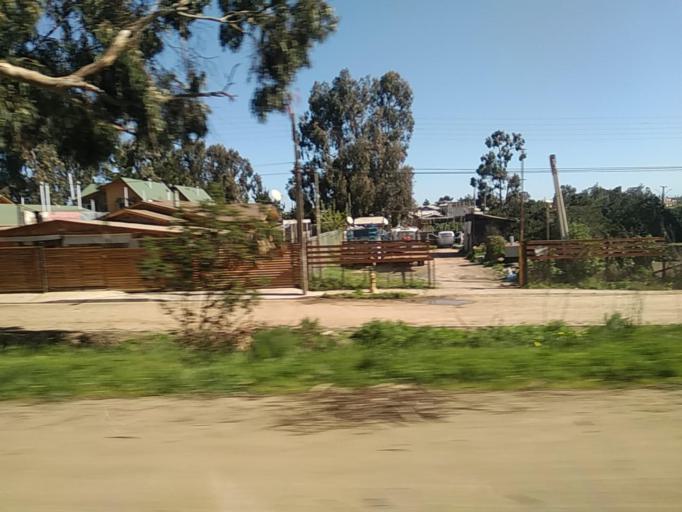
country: CL
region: Valparaiso
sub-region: San Antonio Province
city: El Tabo
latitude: -33.4264
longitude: -71.6912
